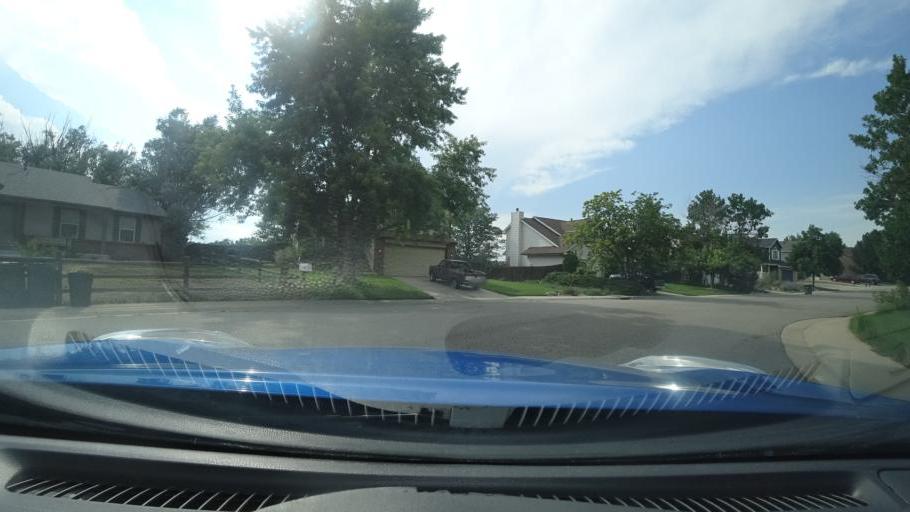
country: US
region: Colorado
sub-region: Adams County
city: Aurora
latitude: 39.6864
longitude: -104.8014
